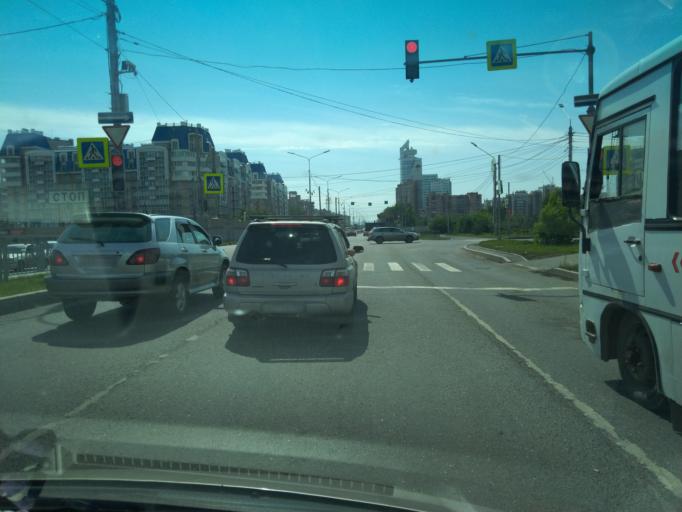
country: RU
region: Krasnoyarskiy
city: Krasnoyarsk
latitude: 56.0477
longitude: 92.9173
